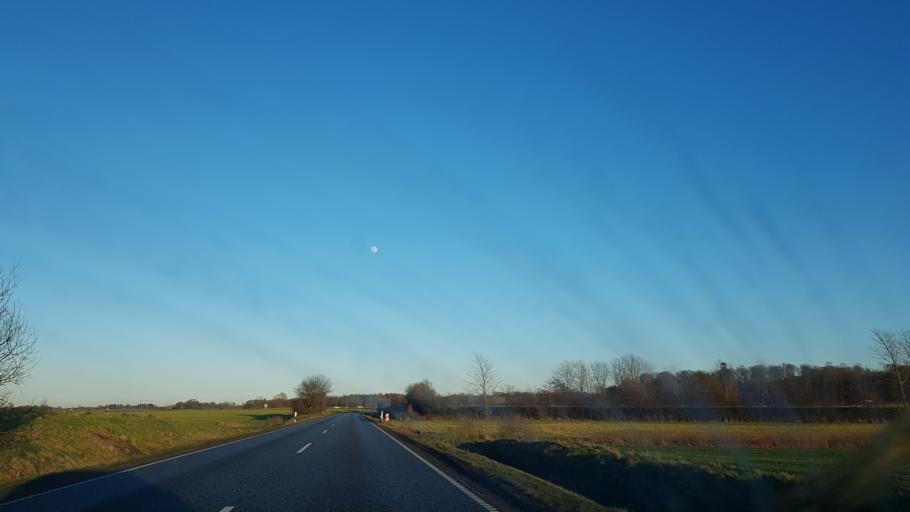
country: DK
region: South Denmark
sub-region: Kolding Kommune
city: Kolding
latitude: 55.4347
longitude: 9.4676
